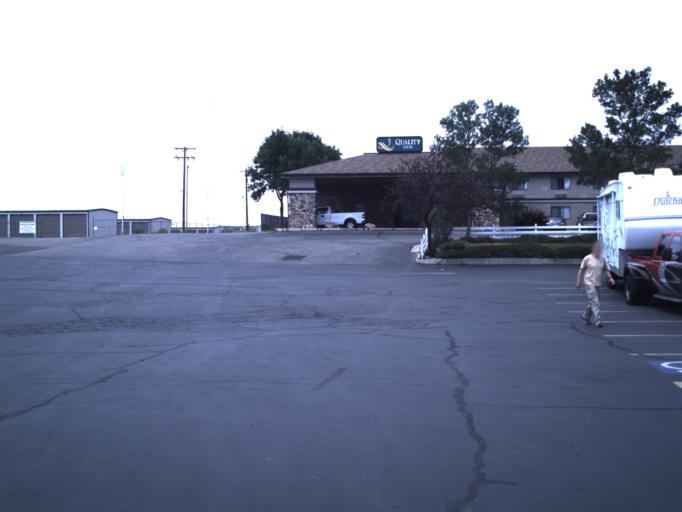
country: US
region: Utah
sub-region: Beaver County
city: Beaver
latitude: 38.2492
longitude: -112.6532
